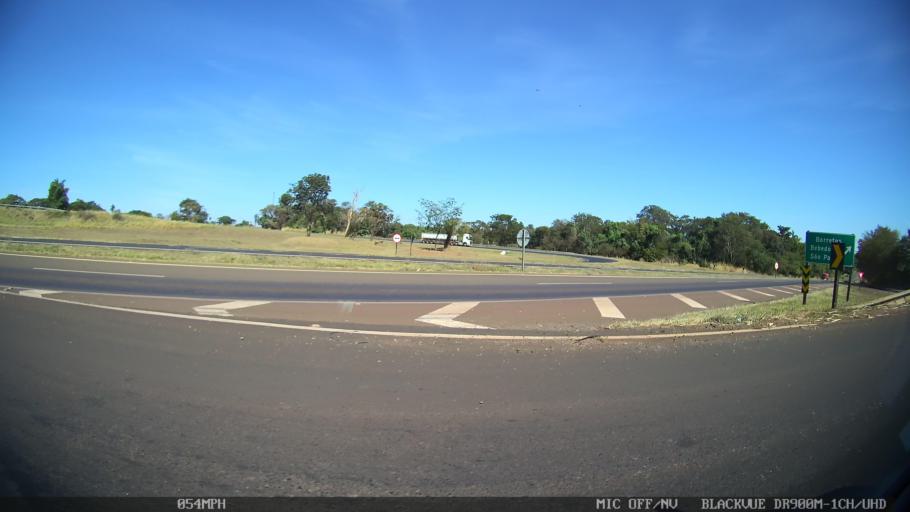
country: BR
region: Sao Paulo
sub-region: Barretos
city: Barretos
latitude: -20.5315
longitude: -48.5993
